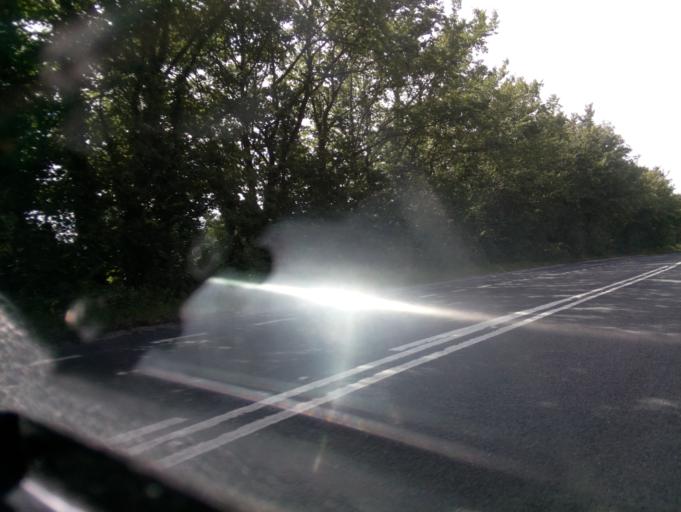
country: GB
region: England
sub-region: Dorset
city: Dorchester
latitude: 50.7566
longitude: -2.5219
